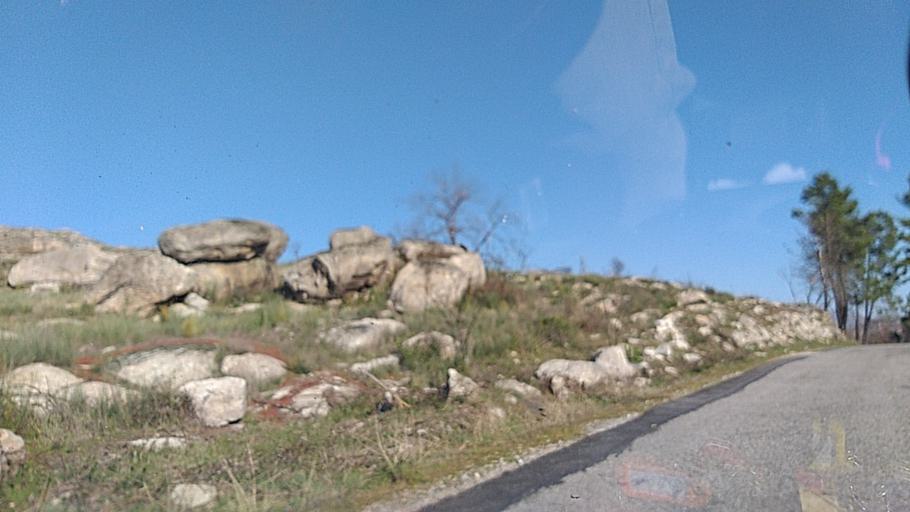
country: PT
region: Guarda
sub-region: Celorico da Beira
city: Celorico da Beira
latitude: 40.6701
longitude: -7.4575
